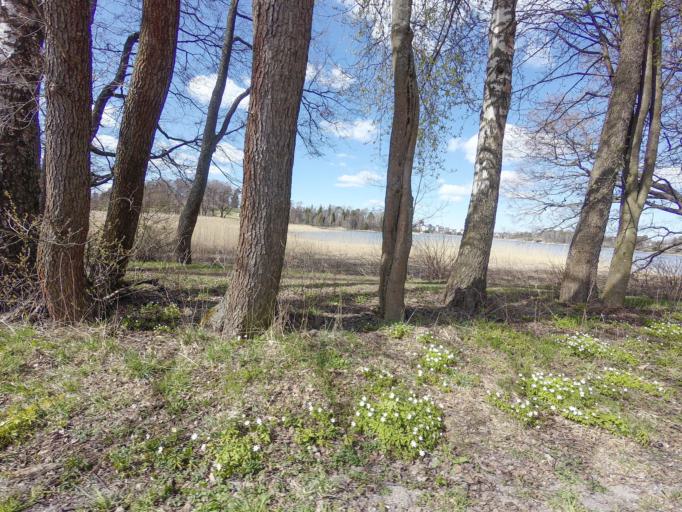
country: FI
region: Uusimaa
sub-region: Helsinki
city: Helsinki
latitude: 60.1793
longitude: 25.0398
